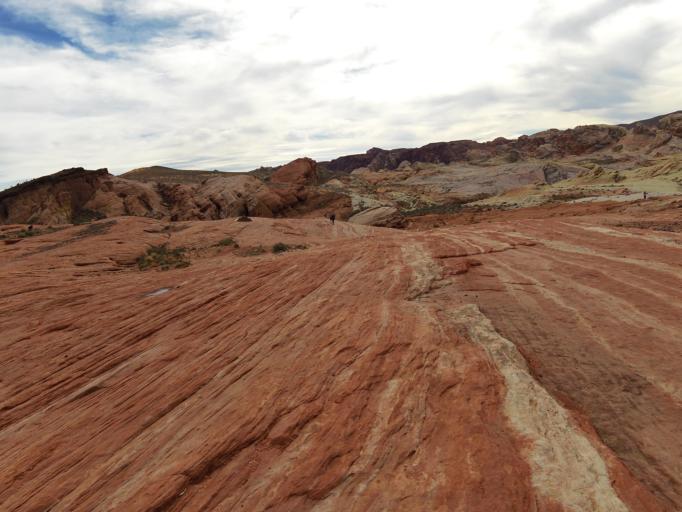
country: US
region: Nevada
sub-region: Clark County
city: Moapa Valley
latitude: 36.4840
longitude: -114.5224
